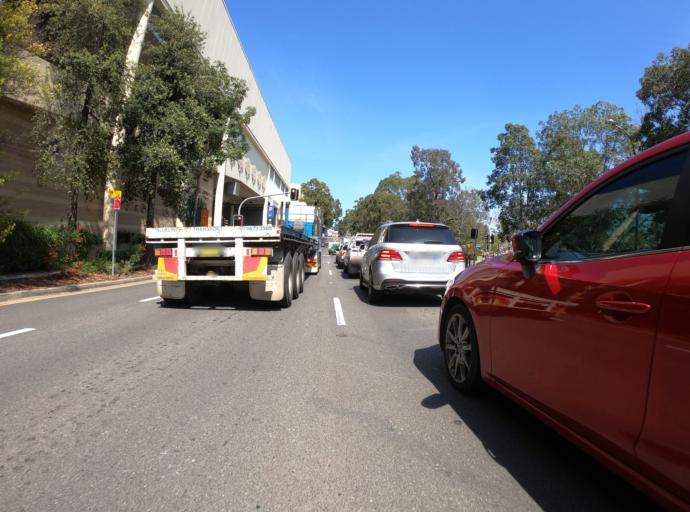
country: AU
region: New South Wales
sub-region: The Hills Shire
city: Castle Hill
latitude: -33.7290
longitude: 151.0061
